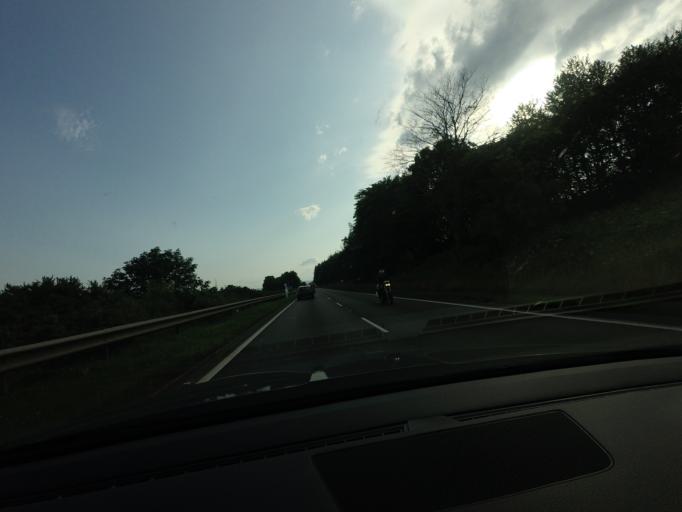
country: GB
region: Scotland
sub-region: Highland
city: Evanton
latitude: 57.6426
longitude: -4.3463
